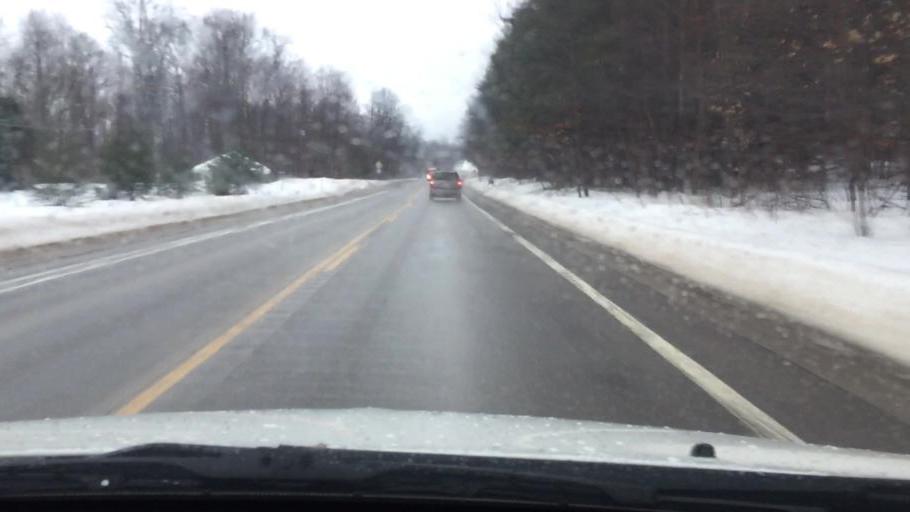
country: US
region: Michigan
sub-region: Charlevoix County
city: East Jordan
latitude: 45.2038
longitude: -85.1651
